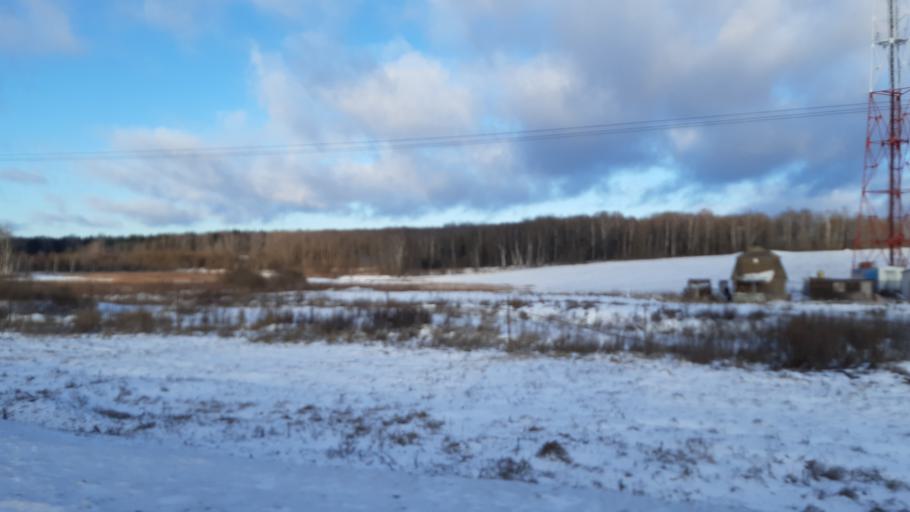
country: RU
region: Moskovskaya
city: Svatkovo
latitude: 56.3127
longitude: 38.3134
